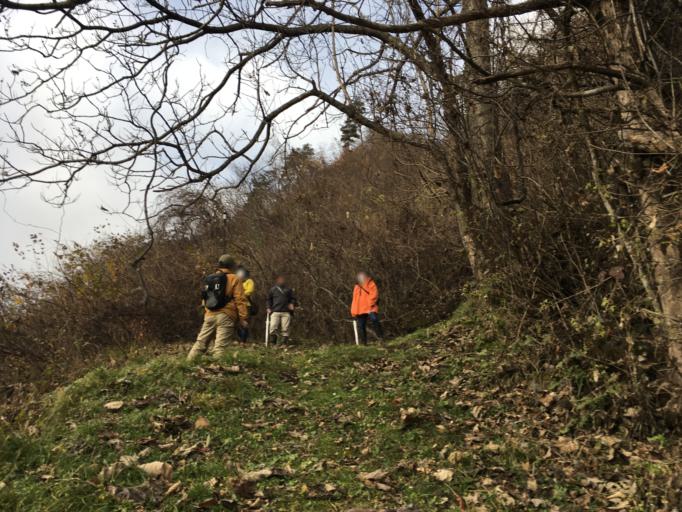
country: JP
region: Iwate
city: Ichinoseki
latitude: 38.9741
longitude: 140.9727
